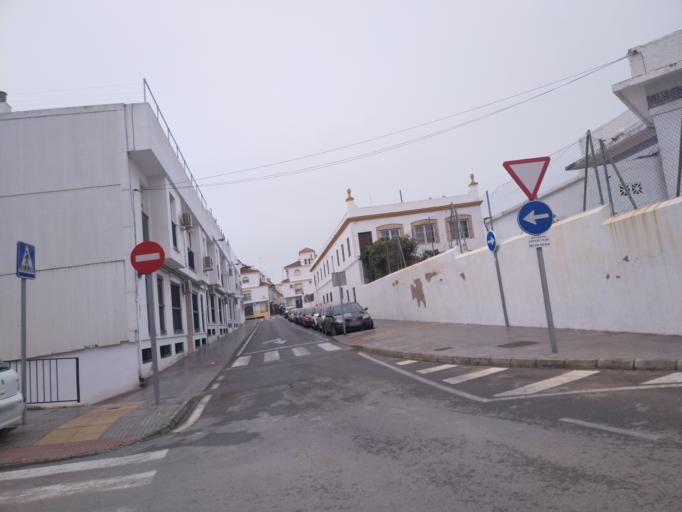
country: ES
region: Andalusia
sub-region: Provincia de Cadiz
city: San Fernando
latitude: 36.4775
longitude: -6.1970
